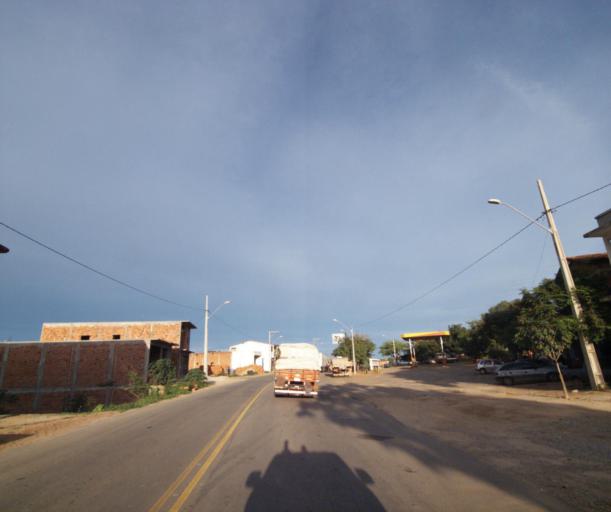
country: BR
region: Bahia
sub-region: Cacule
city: Cacule
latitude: -14.2051
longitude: -42.1194
